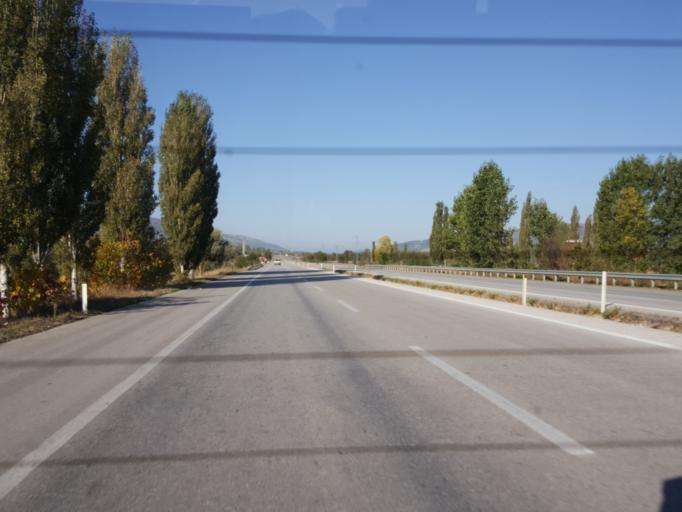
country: TR
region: Amasya
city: Ezinepazari
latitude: 40.5704
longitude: 36.0945
